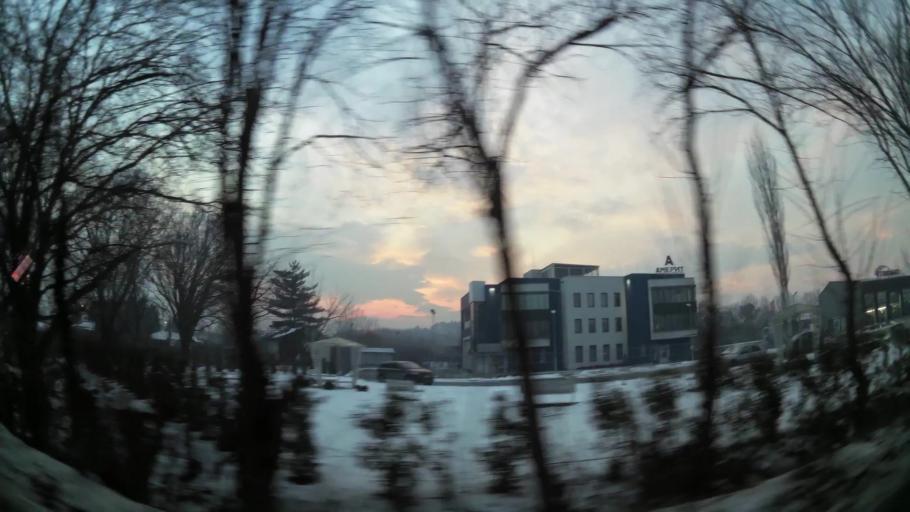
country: MK
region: Suto Orizari
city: Suto Orizare
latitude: 42.0169
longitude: 21.4108
